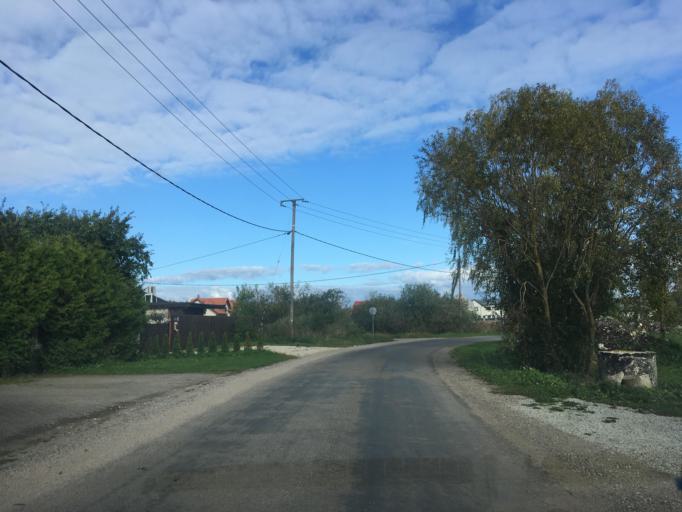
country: EE
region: Harju
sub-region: Joelaehtme vald
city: Loo
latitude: 59.4452
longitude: 24.9724
